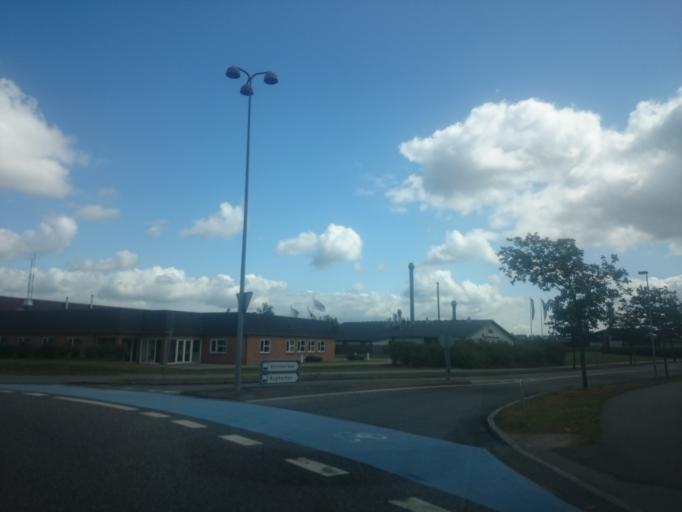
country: DK
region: South Denmark
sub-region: Billund Kommune
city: Billund
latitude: 55.7165
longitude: 9.1292
